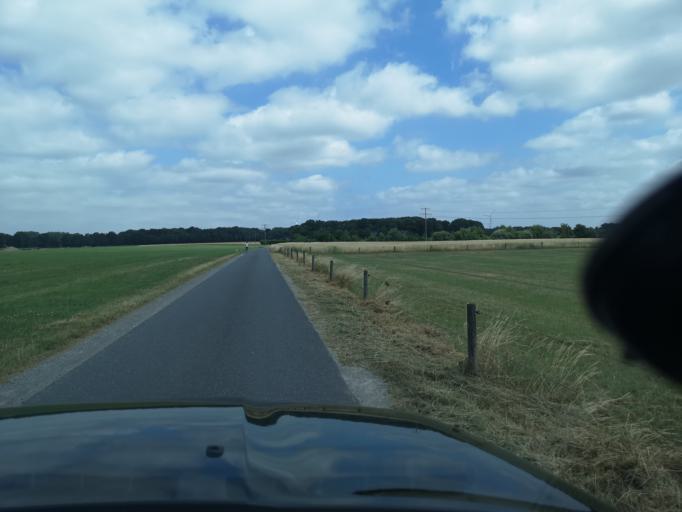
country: DE
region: North Rhine-Westphalia
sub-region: Regierungsbezirk Munster
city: Rhede
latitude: 51.8467
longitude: 6.6812
